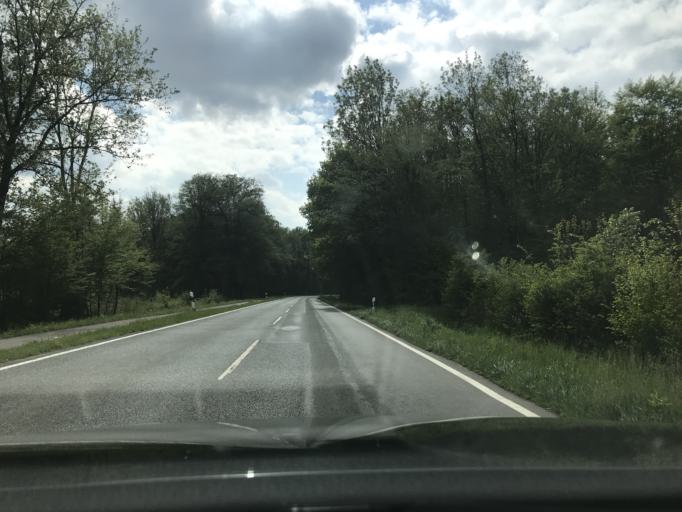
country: DE
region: North Rhine-Westphalia
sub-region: Regierungsbezirk Detmold
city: Rheda-Wiedenbruck
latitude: 51.8357
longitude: 8.2303
